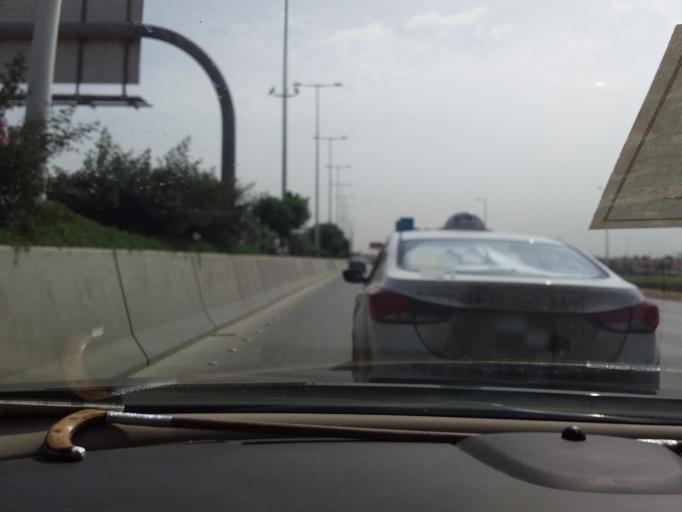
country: SA
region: Ar Riyad
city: Riyadh
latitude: 24.7291
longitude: 46.7095
